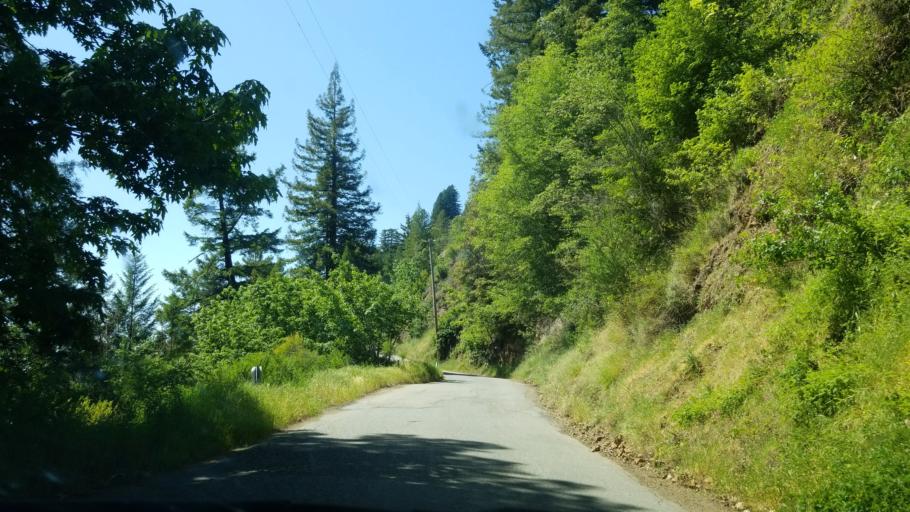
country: US
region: California
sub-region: Santa Cruz County
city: Day Valley
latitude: 37.0861
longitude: -121.8595
